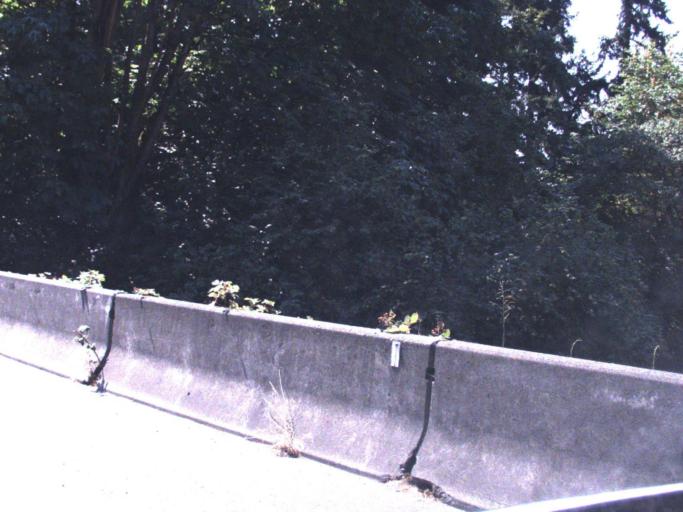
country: US
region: Washington
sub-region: King County
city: Redmond
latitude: 47.6875
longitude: -122.1284
